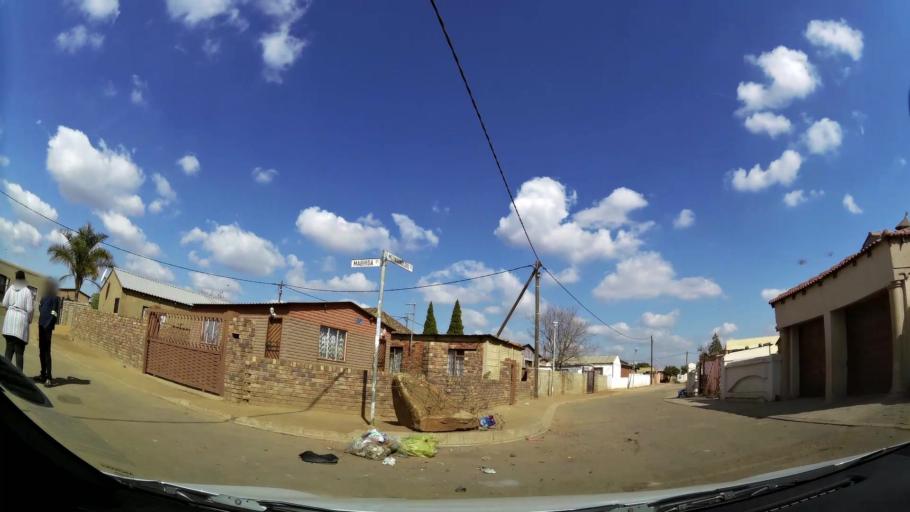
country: ZA
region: Gauteng
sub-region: City of Tshwane Metropolitan Municipality
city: Cullinan
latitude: -25.7098
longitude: 28.4104
